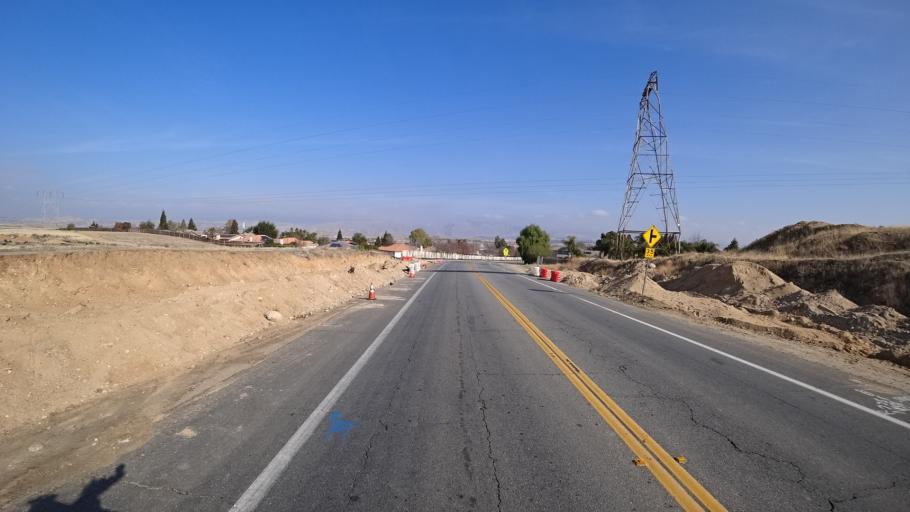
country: US
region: California
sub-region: Kern County
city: Oildale
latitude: 35.4034
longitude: -118.9208
